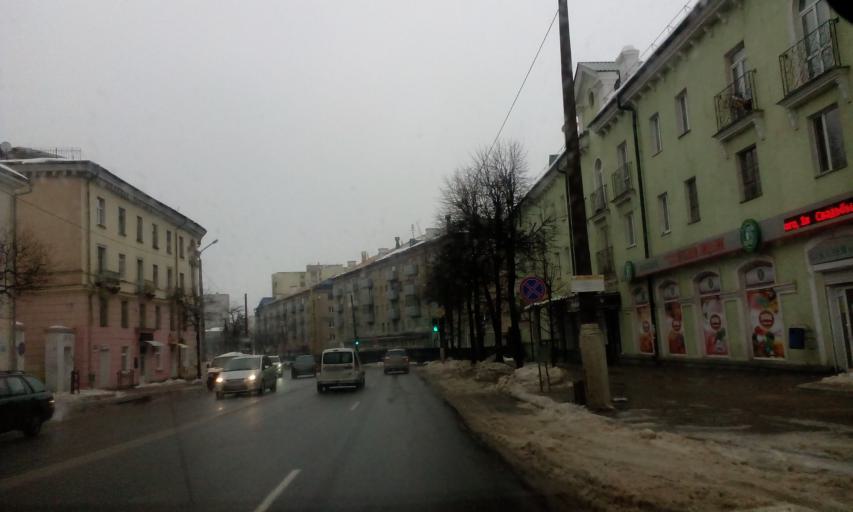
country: BY
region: Mogilev
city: Mahilyow
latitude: 53.9028
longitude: 30.3438
